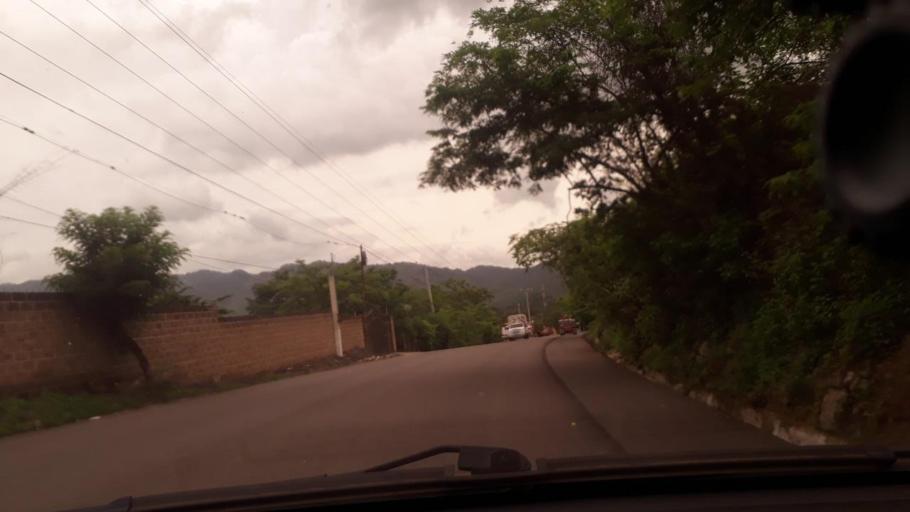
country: GT
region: Chiquimula
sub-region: Municipio de San Juan Ermita
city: San Juan Ermita
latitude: 14.7347
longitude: -89.4826
